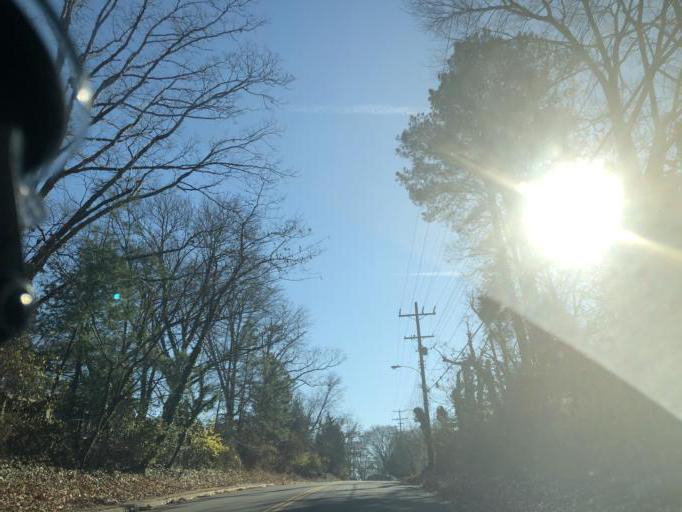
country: US
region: Virginia
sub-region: Fairfax County
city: Baileys Crossroads
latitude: 38.8400
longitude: -77.1298
